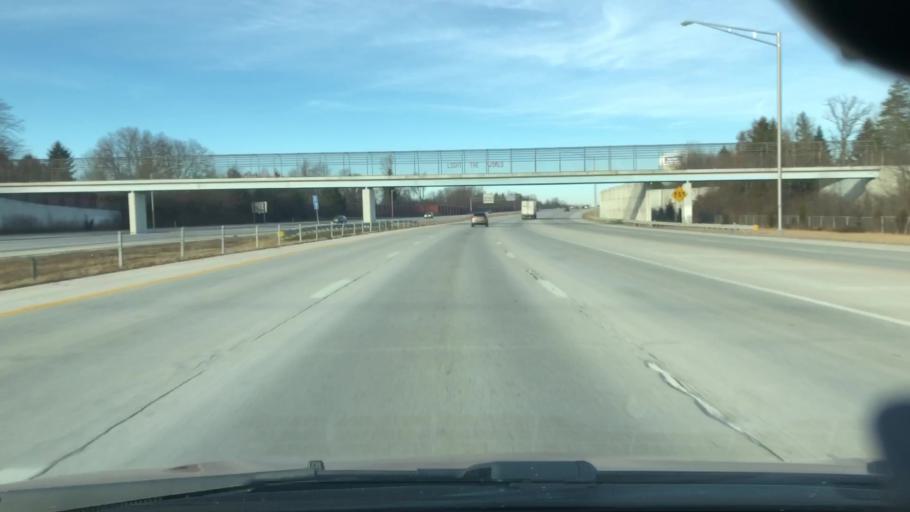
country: US
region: Ohio
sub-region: Greene County
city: Beavercreek
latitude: 39.7410
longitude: -84.0942
